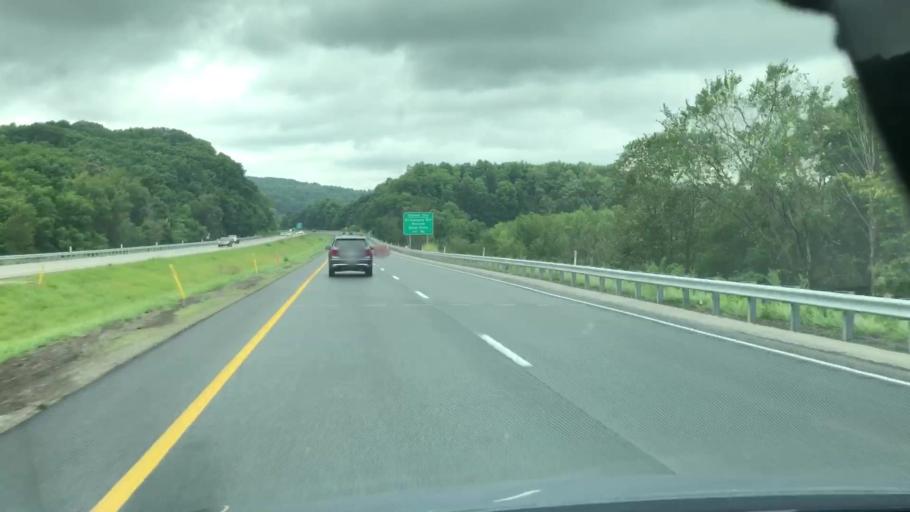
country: US
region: Pennsylvania
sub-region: Butler County
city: Prospect
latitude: 40.9005
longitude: -80.1229
